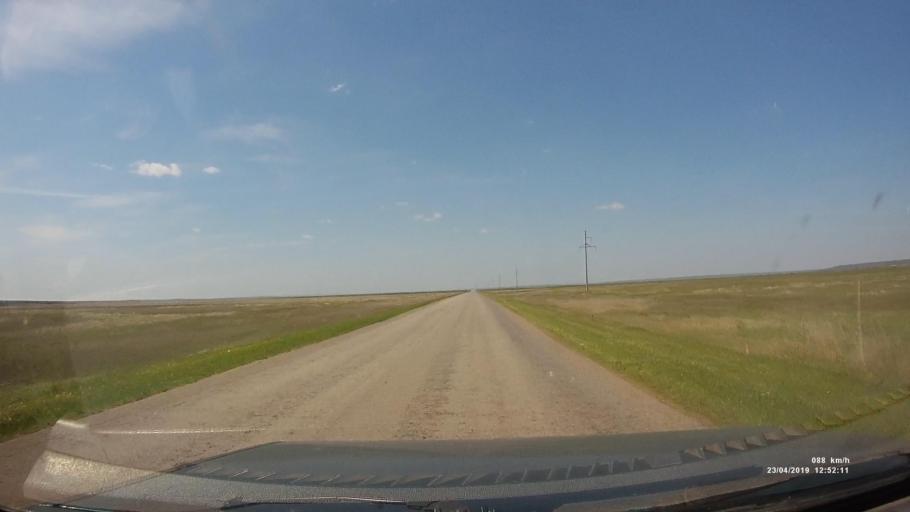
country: RU
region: Kalmykiya
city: Yashalta
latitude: 46.5622
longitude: 42.6129
